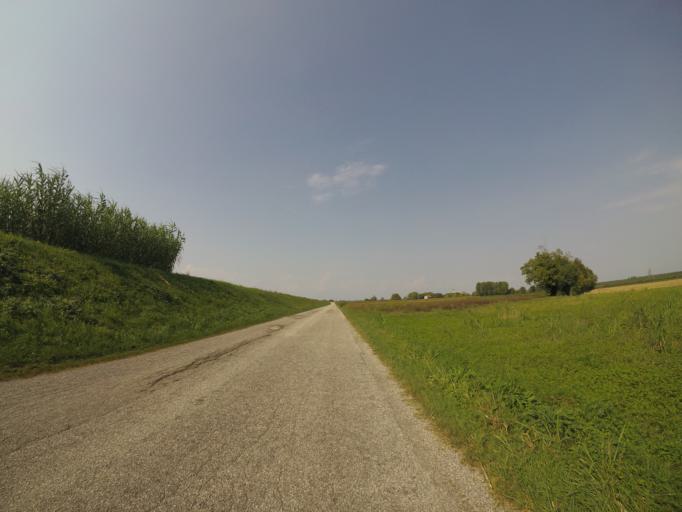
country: IT
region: Friuli Venezia Giulia
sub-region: Provincia di Udine
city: Camino al Tagliamento
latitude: 45.9114
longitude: 12.9308
